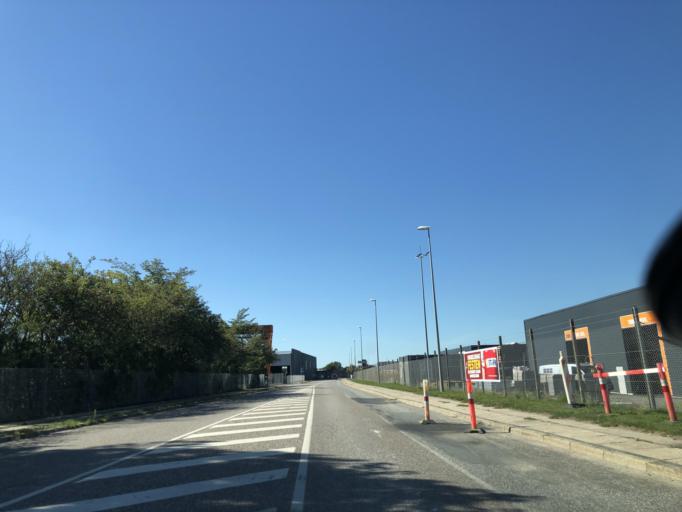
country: DK
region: North Denmark
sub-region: Mariagerfjord Kommune
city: Hobro
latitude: 56.6496
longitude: 9.8012
